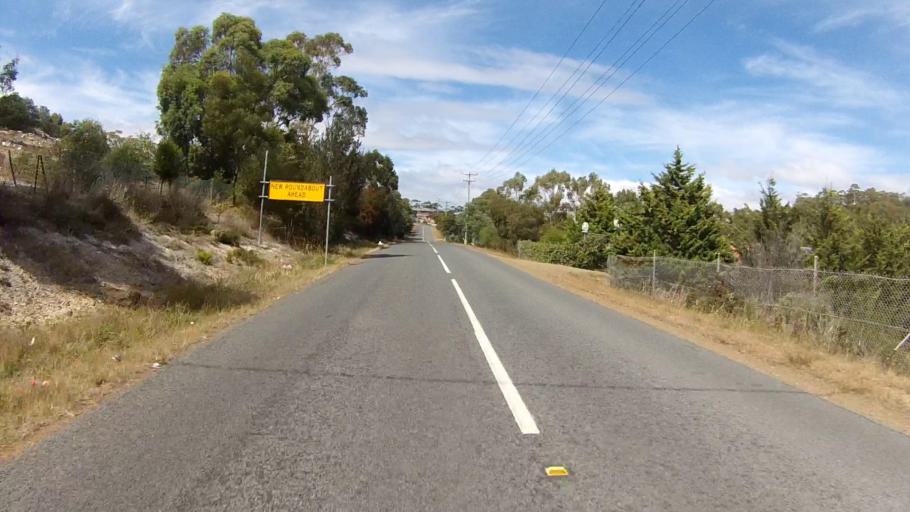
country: AU
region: Tasmania
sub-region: Clarence
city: Lindisfarne
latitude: -42.8181
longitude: 147.3513
